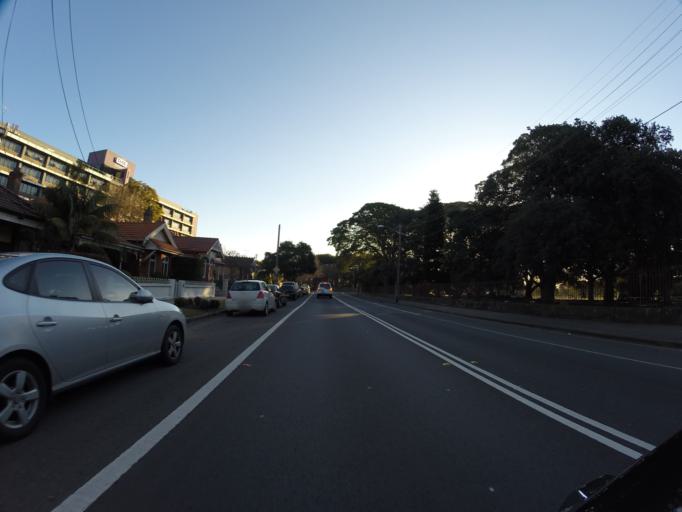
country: AU
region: New South Wales
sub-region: Woollahra
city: Woollahra
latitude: -33.9050
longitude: 151.2337
